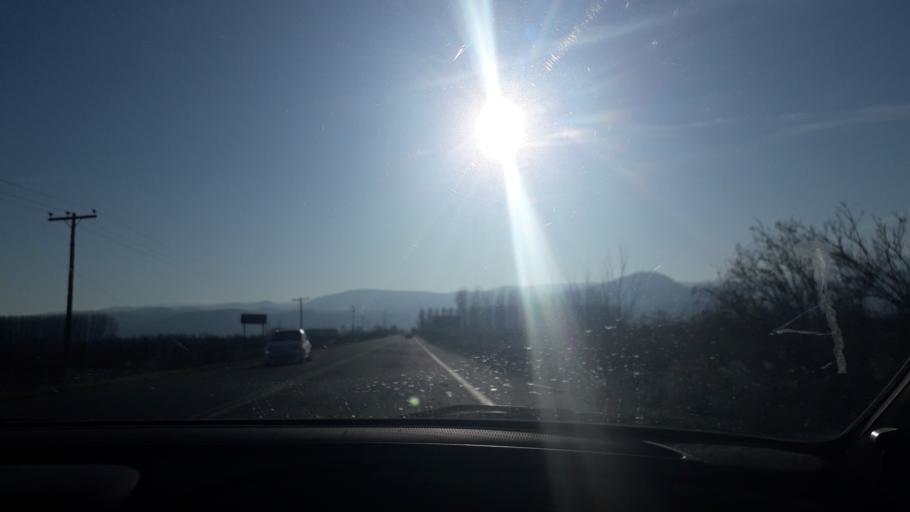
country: GR
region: Central Macedonia
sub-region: Nomos Pellis
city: Apsalos
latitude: 40.9190
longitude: 22.0781
